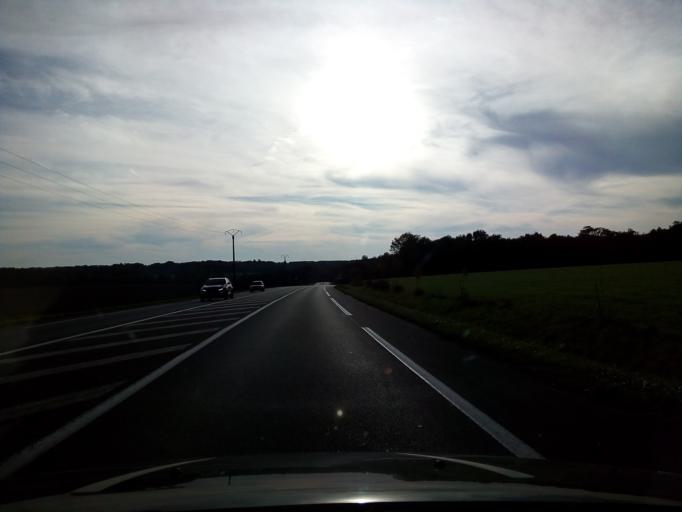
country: FR
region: Poitou-Charentes
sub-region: Departement de la Charente
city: Loubert
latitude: 45.9676
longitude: 0.5873
